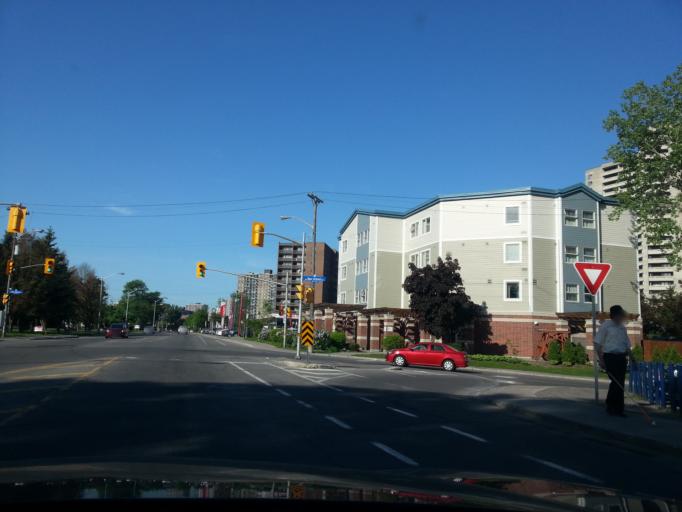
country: CA
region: Ontario
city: Bells Corners
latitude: 45.3740
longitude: -75.7785
